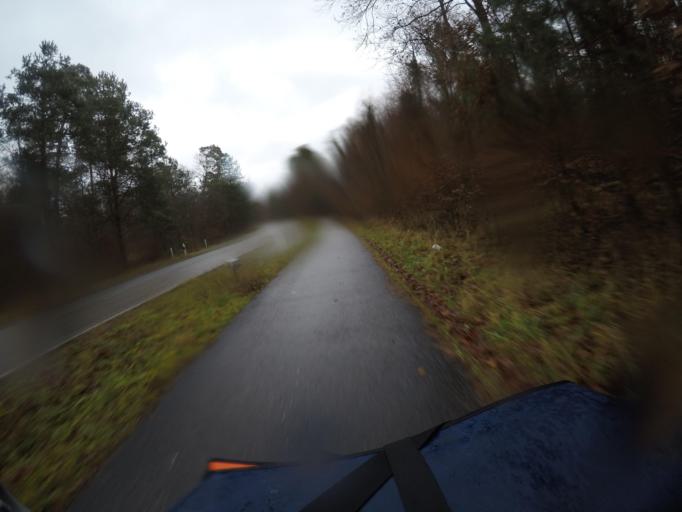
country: DE
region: Baden-Wuerttemberg
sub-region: Karlsruhe Region
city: Linkenheim-Hochstetten
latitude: 49.1108
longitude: 8.4606
